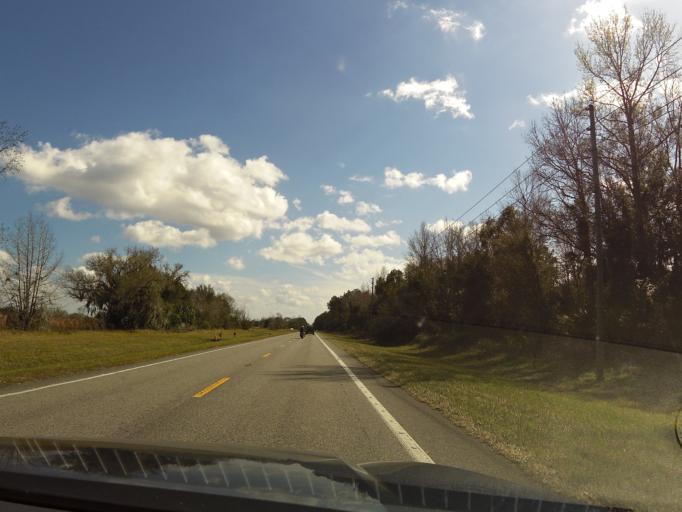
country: US
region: Florida
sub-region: Volusia County
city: De Leon Springs
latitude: 29.1617
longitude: -81.3884
